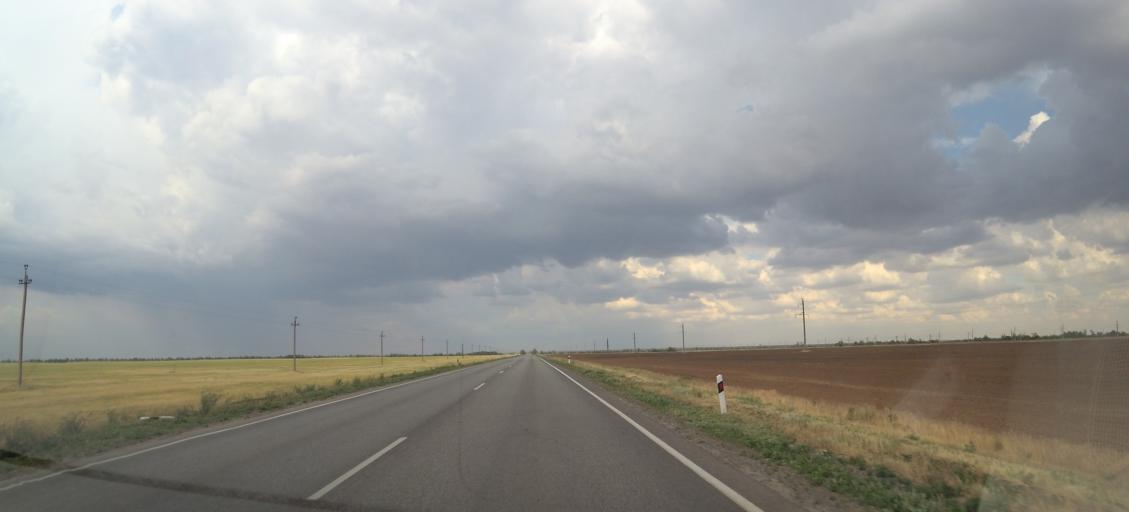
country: RU
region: Rostov
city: Zimovniki
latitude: 47.1202
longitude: 42.3899
